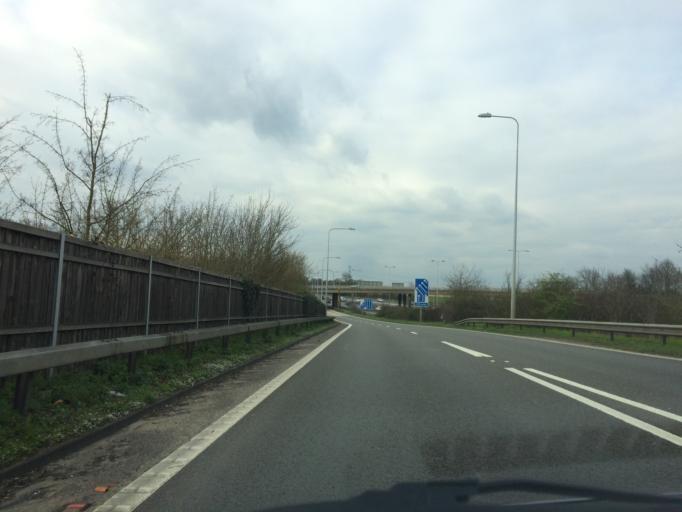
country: GB
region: England
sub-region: Surrey
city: Chertsey
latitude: 51.3757
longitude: -0.5103
